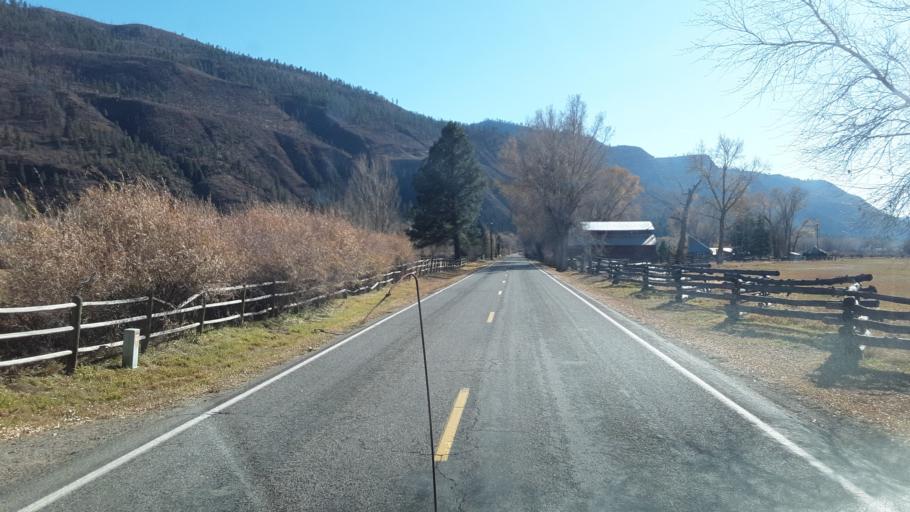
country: US
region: Colorado
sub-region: La Plata County
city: Durango
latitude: 37.4296
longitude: -107.7996
